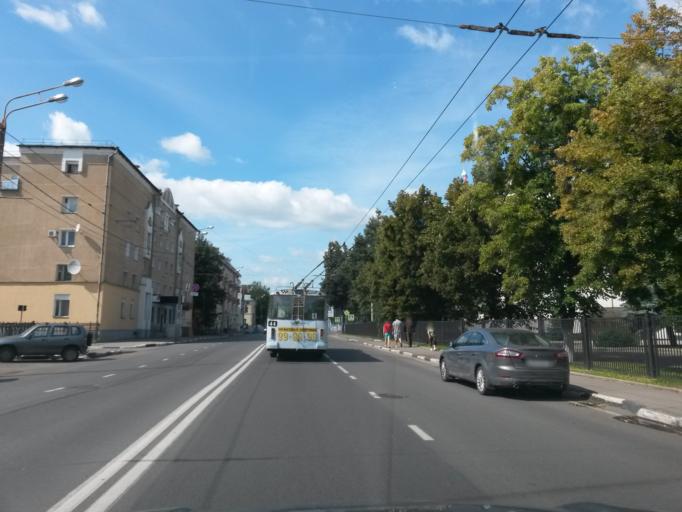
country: RU
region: Jaroslavl
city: Yaroslavl
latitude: 57.6336
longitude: 39.8851
